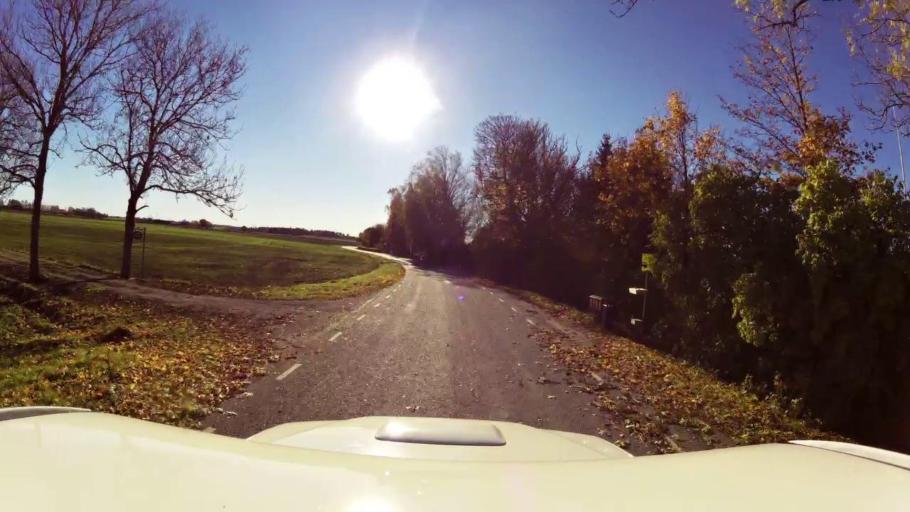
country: SE
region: OEstergoetland
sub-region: Linkopings Kommun
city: Ljungsbro
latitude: 58.4844
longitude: 15.4183
